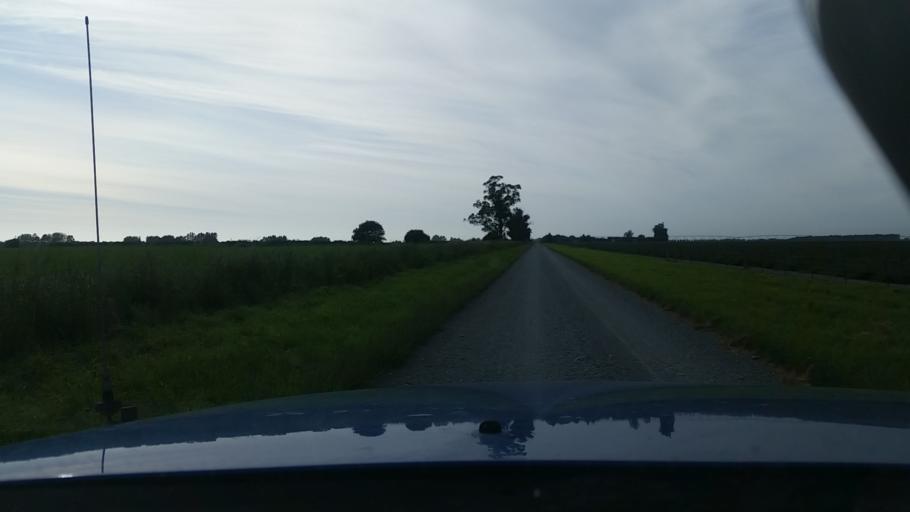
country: NZ
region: Canterbury
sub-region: Ashburton District
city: Tinwald
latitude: -44.0019
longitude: 171.8020
